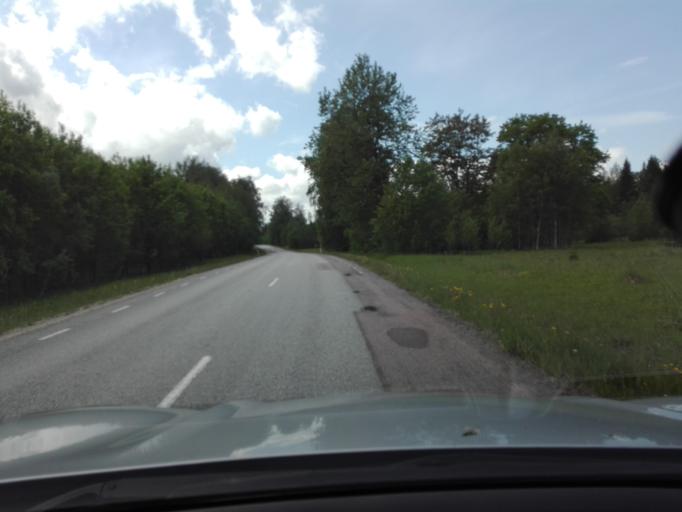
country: EE
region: Raplamaa
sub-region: Rapla vald
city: Rapla
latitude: 59.0187
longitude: 24.8293
